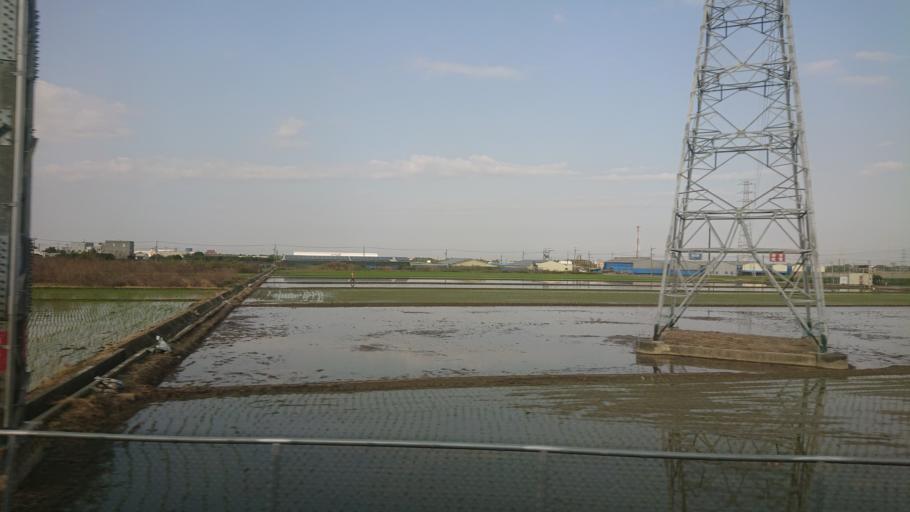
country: TW
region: Taiwan
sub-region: Chiayi
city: Jiayi Shi
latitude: 23.5749
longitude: 120.4370
